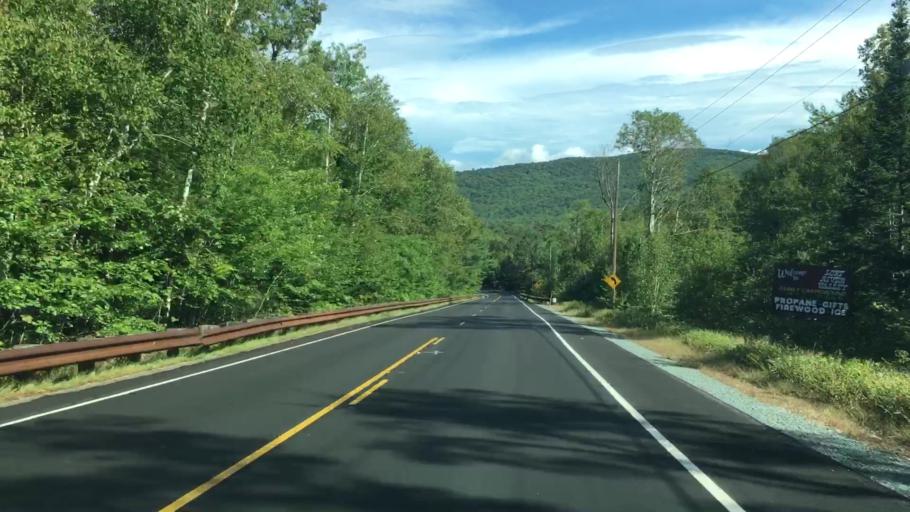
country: US
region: New Hampshire
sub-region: Grafton County
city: Woodstock
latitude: 44.0206
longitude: -71.7472
